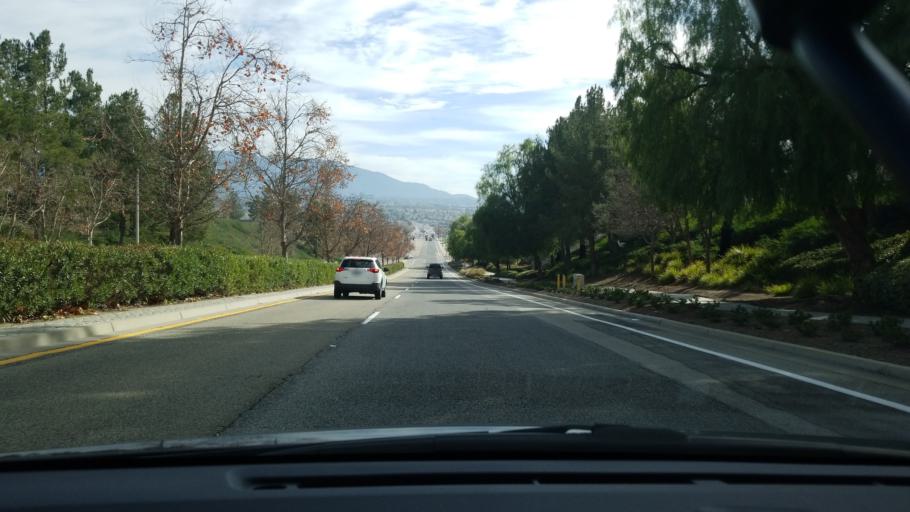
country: US
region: California
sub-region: Riverside County
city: Temecula
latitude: 33.4920
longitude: -117.0815
